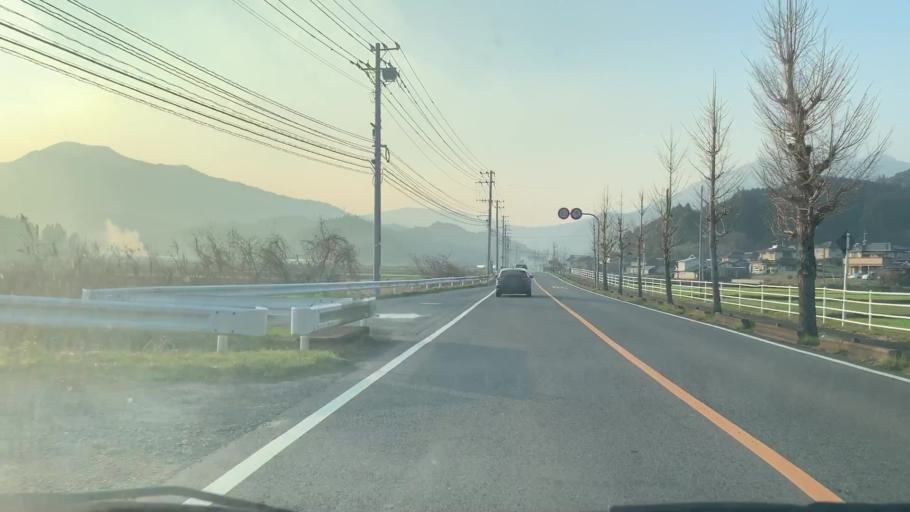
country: JP
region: Saga Prefecture
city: Takeocho-takeo
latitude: 33.2579
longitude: 130.0715
